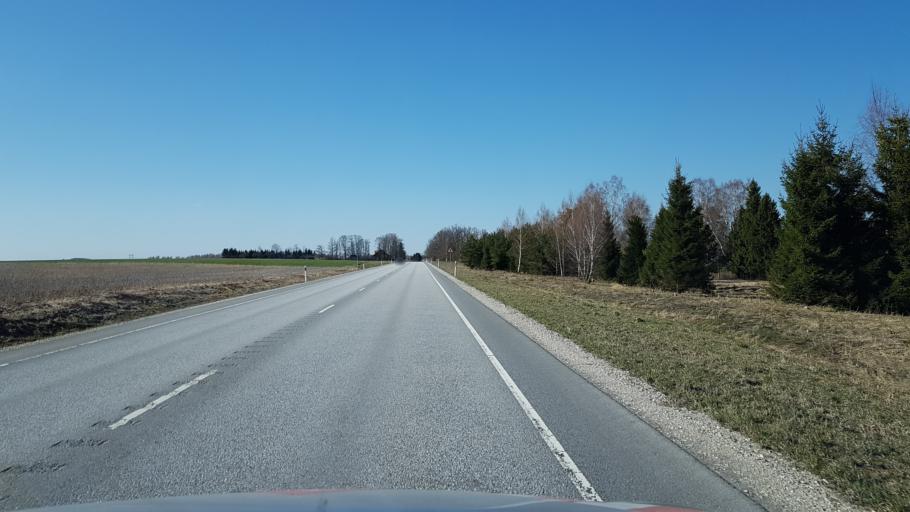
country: EE
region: Tartu
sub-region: Tartu linn
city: Tartu
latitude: 58.5408
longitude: 26.7628
